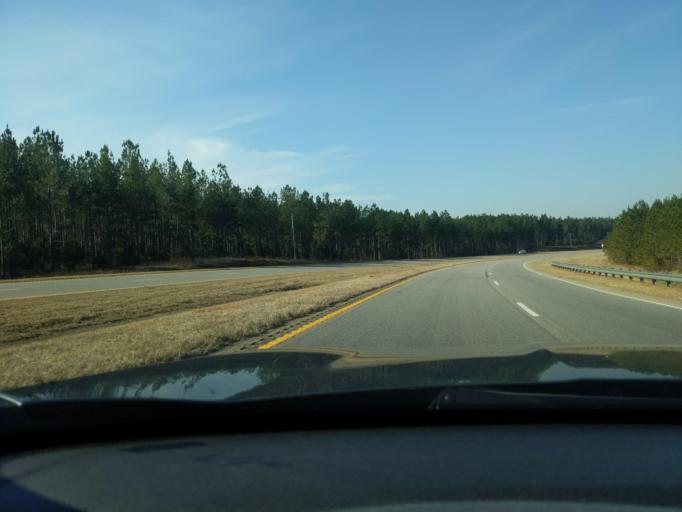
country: US
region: South Carolina
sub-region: Abbeville County
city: Abbeville
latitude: 34.1136
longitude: -82.4681
